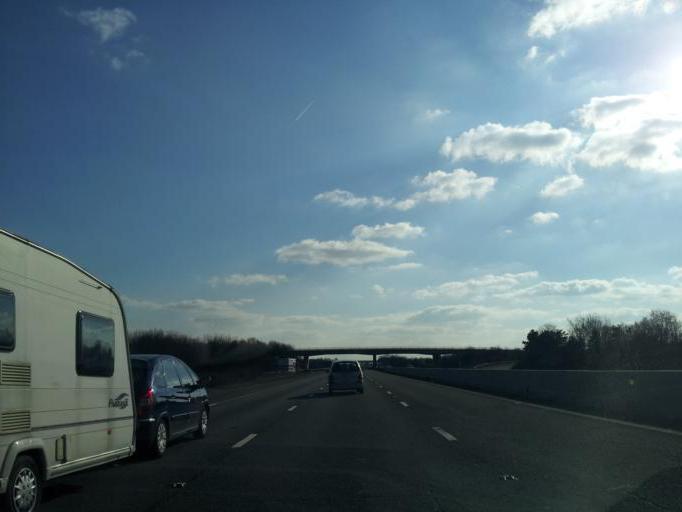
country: GB
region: England
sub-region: Somerset
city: Highbridge
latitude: 51.2377
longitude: -2.9451
